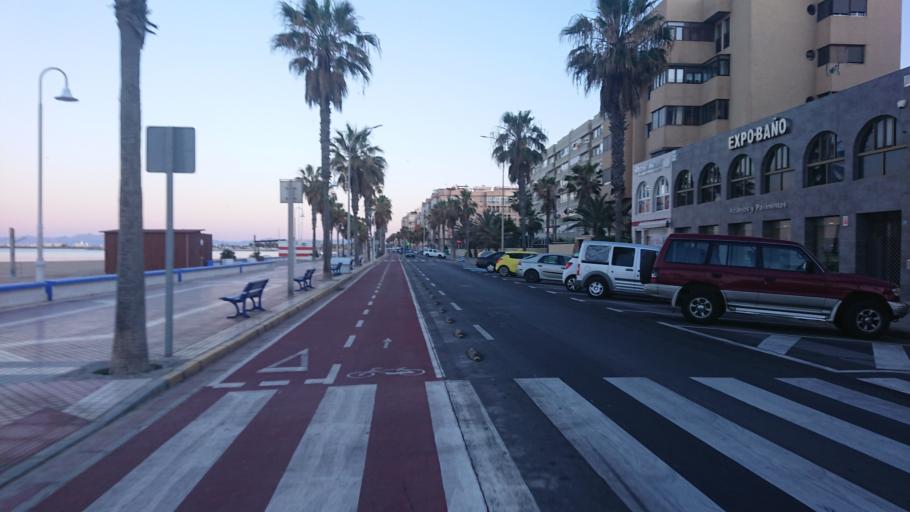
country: ES
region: Melilla
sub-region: Melilla
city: Melilla
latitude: 35.2830
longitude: -2.9383
